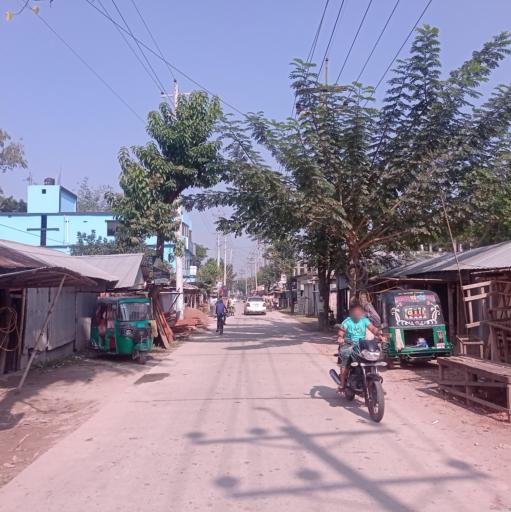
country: BD
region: Dhaka
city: Narsingdi
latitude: 24.0665
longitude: 90.6913
